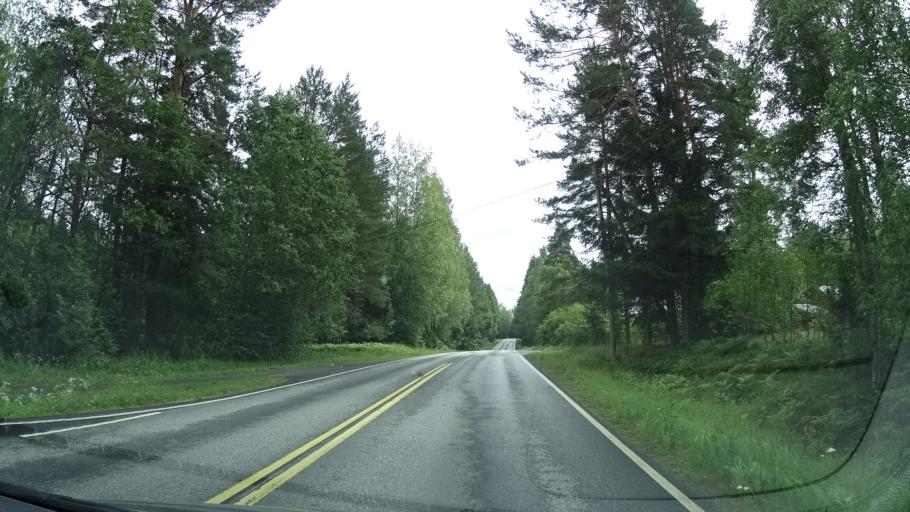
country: FI
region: Pirkanmaa
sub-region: Etelae-Pirkanmaa
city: Urjala
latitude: 61.0892
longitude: 23.3950
